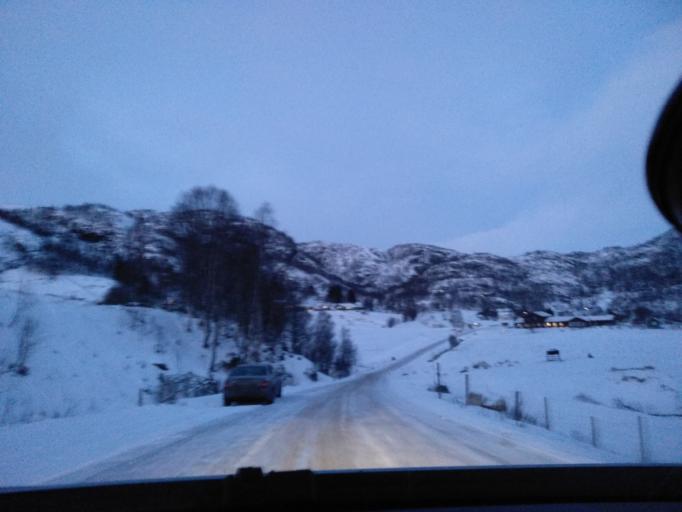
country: NO
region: Vest-Agder
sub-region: Sirdal
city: Tonstad
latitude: 59.0199
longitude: 6.9227
